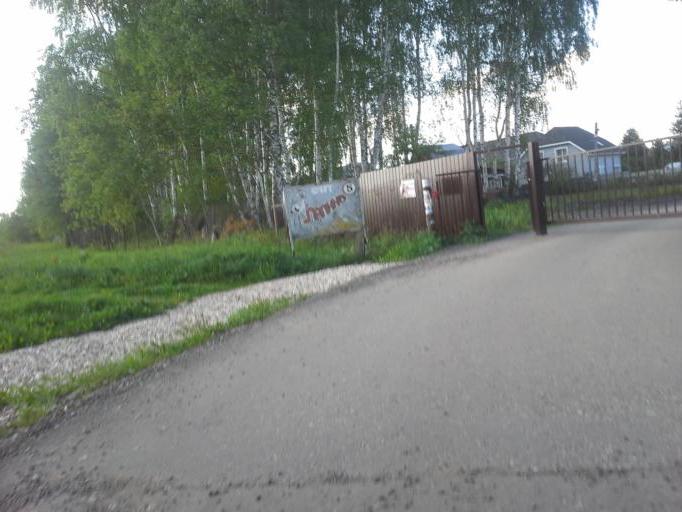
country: RU
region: Moskovskaya
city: Zhavoronki
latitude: 55.6655
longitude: 37.1395
